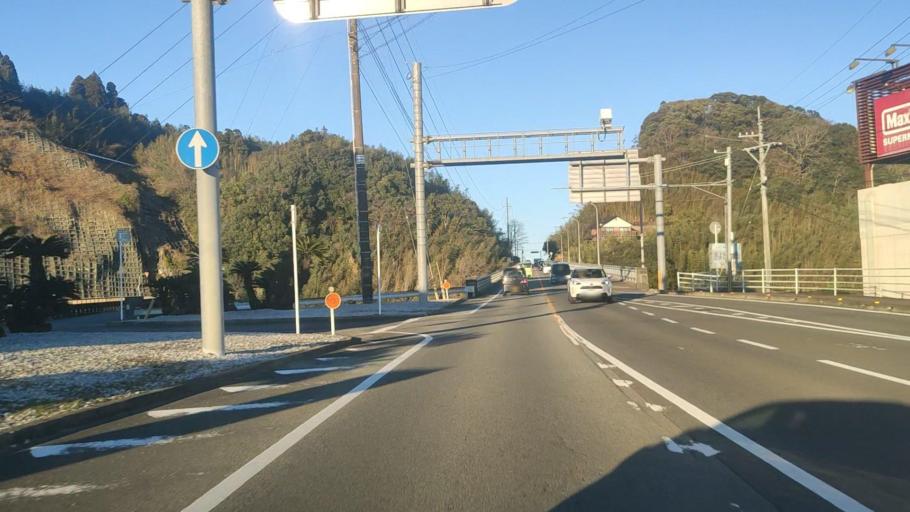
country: JP
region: Miyazaki
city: Miyazaki-shi
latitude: 31.8622
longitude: 131.3863
